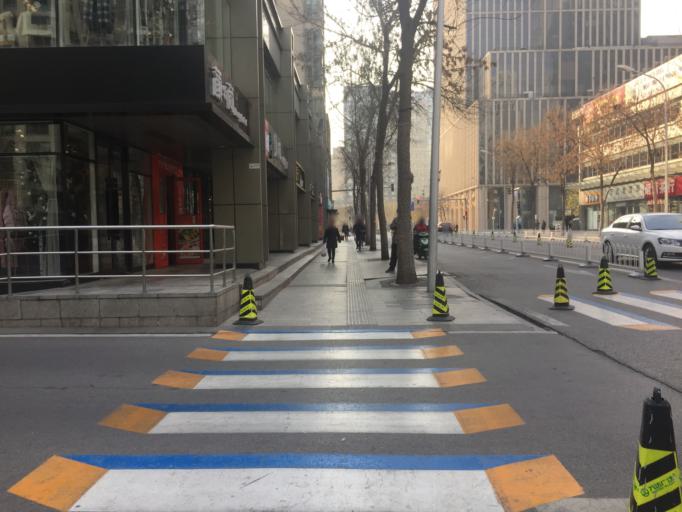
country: CN
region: Beijing
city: Chaowai
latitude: 39.9095
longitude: 116.4655
